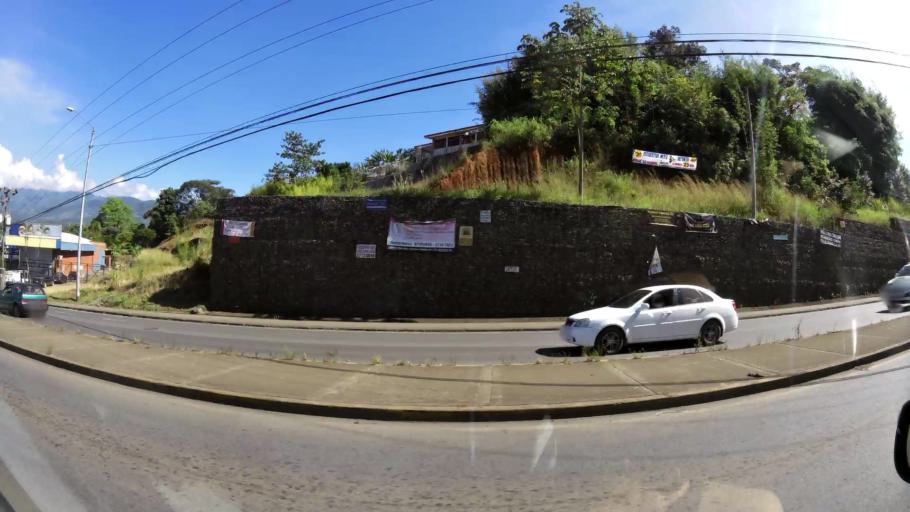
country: CR
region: San Jose
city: San Isidro
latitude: 9.3678
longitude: -83.6983
